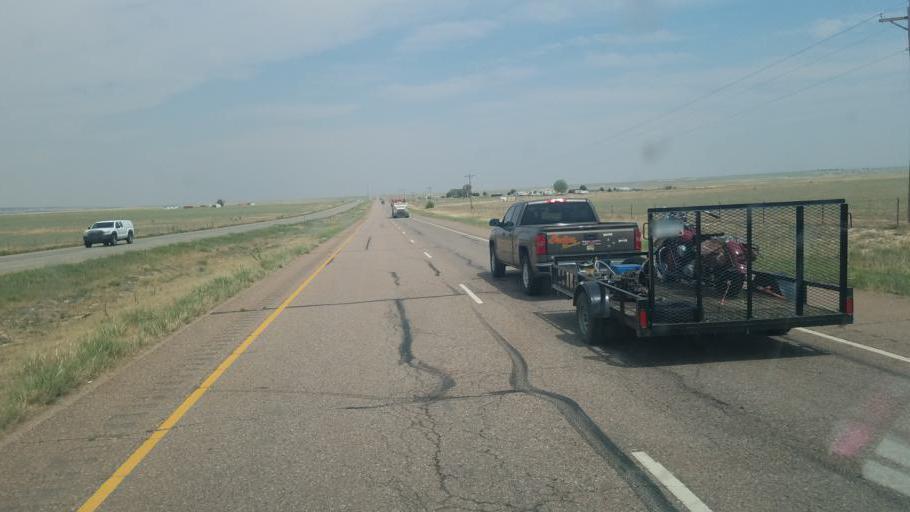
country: US
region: Colorado
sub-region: Fremont County
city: Penrose
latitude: 38.3687
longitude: -104.9213
